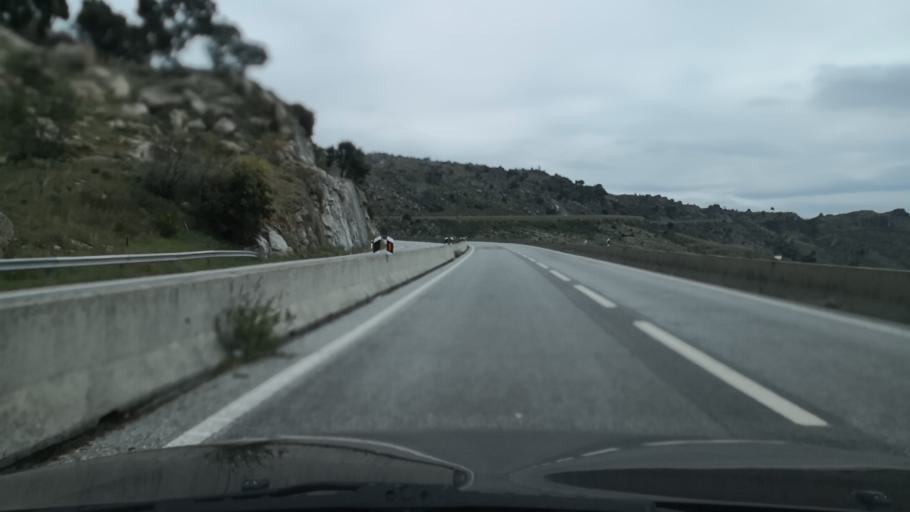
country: PT
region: Guarda
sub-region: Guarda
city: Guarda
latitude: 40.6029
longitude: -7.2816
